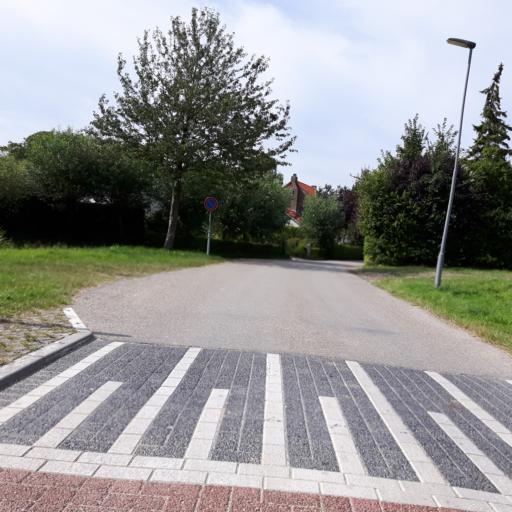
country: NL
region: Zeeland
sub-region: Gemeente Goes
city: Goes
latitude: 51.4681
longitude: 3.8831
